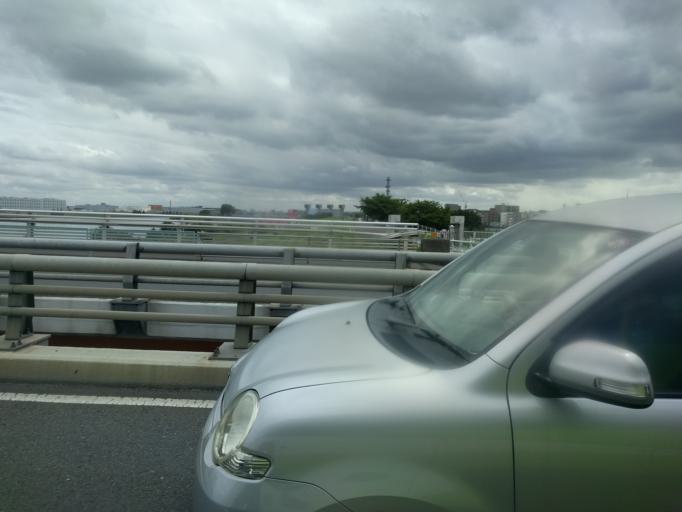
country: JP
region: Saitama
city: Kawaguchi
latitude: 35.7879
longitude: 139.7235
